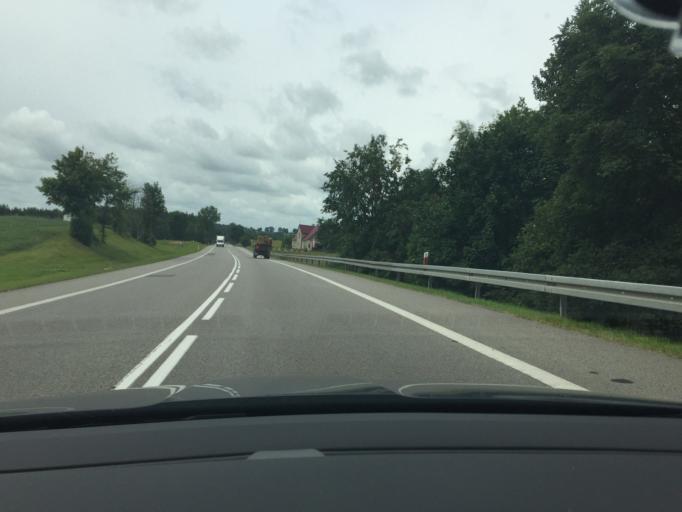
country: PL
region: Pomeranian Voivodeship
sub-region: Powiat starogardzki
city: Smetowo Graniczne
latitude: 53.7425
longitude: 18.7456
